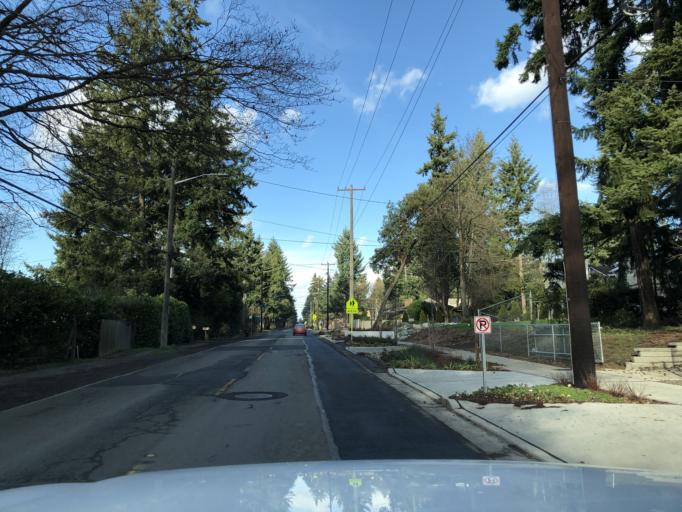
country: US
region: Washington
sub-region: King County
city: Lake Forest Park
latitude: 47.7236
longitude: -122.2963
